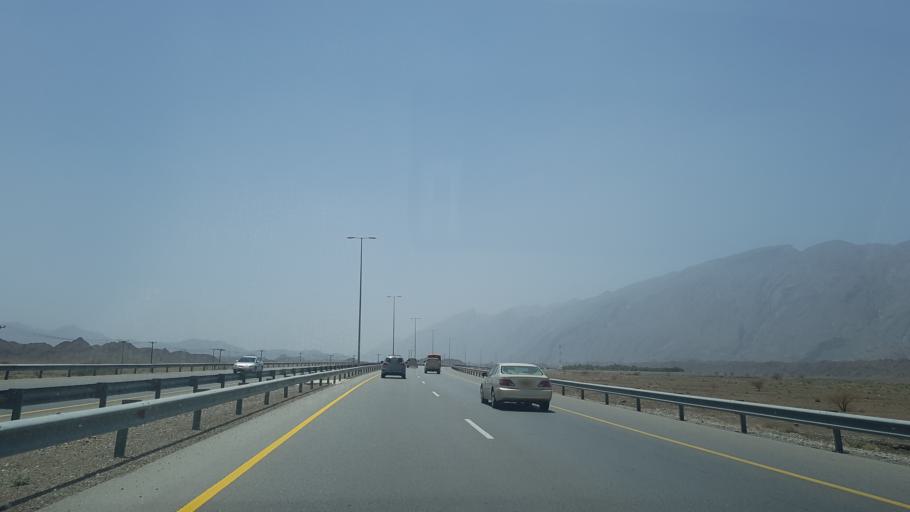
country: OM
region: Muhafazat ad Dakhiliyah
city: Sufalat Sama'il
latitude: 23.2554
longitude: 57.9286
